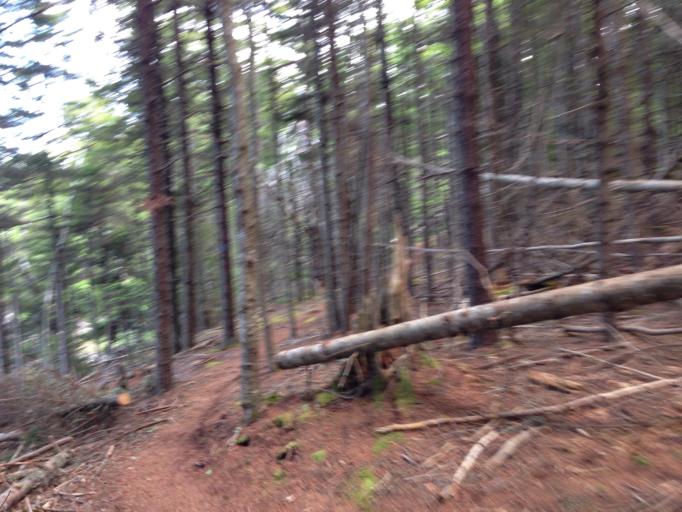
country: US
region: Maine
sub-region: Hancock County
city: Gouldsboro
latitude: 44.3815
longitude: -68.0717
